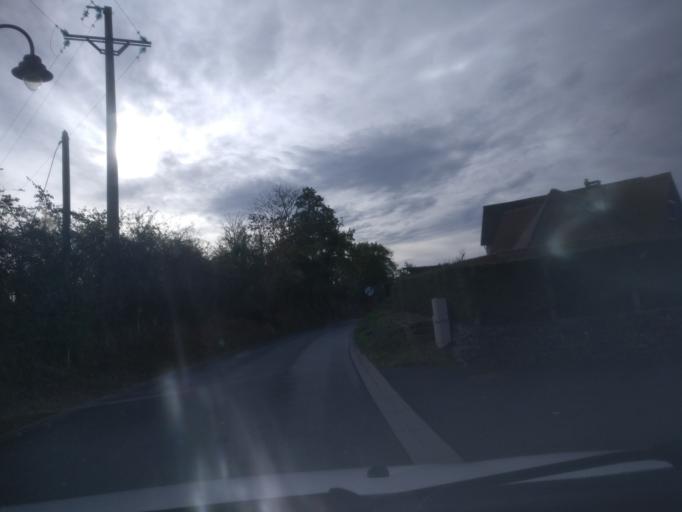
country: FR
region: Lower Normandy
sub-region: Departement de la Manche
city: Jullouville
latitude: 48.7485
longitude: -1.5552
